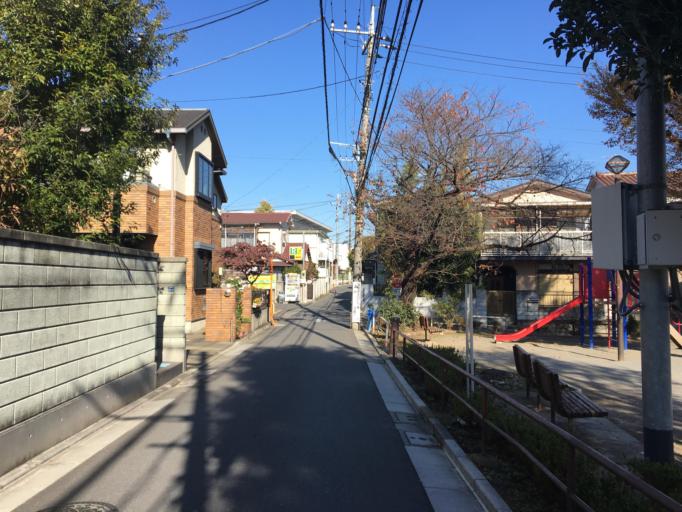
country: JP
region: Saitama
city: Wako
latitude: 35.7861
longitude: 139.6394
